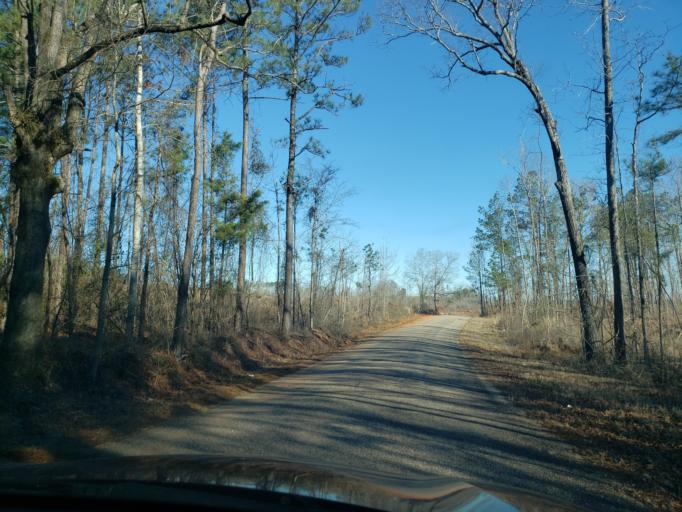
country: US
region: Alabama
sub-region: Elmore County
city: Tallassee
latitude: 32.6630
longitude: -85.8698
